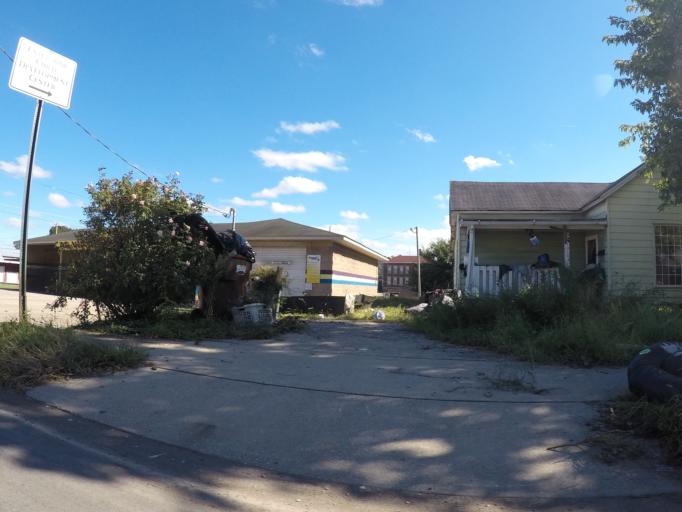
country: US
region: West Virginia
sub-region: Cabell County
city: Huntington
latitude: 38.4097
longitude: -82.4879
